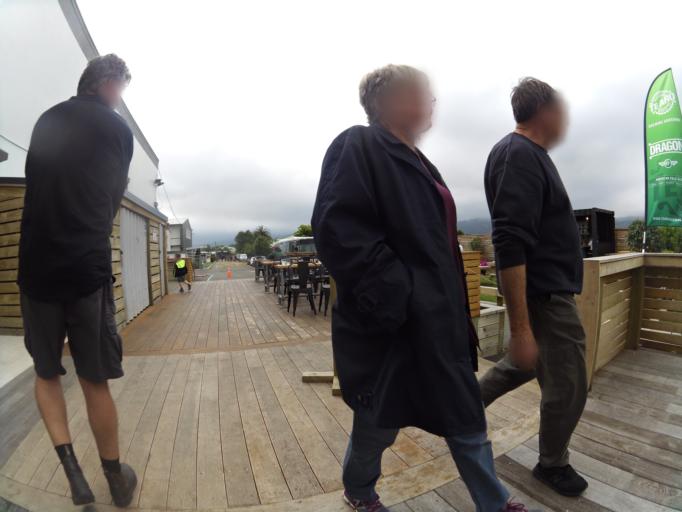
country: NZ
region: Wellington
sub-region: Upper Hutt City
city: Upper Hutt
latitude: -41.1302
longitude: 175.0686
